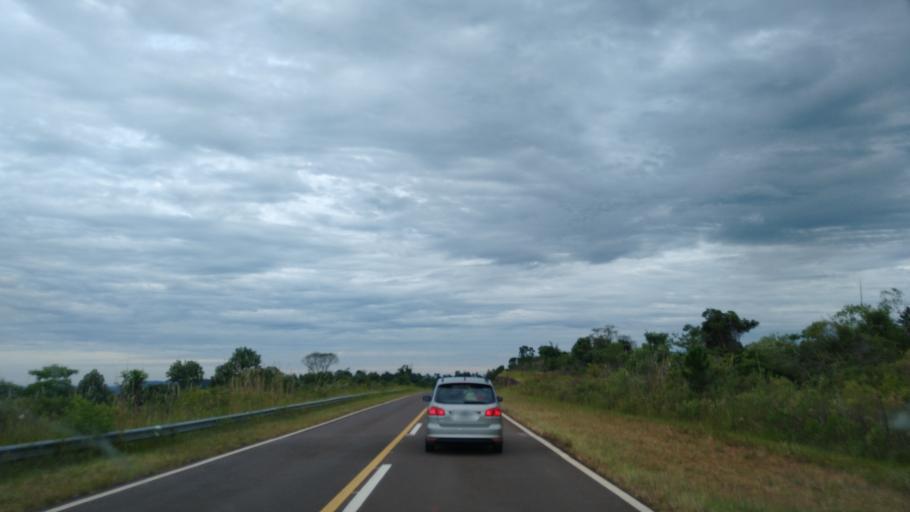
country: AR
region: Misiones
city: Bernardo de Irigoyen
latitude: -26.4132
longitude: -53.8235
